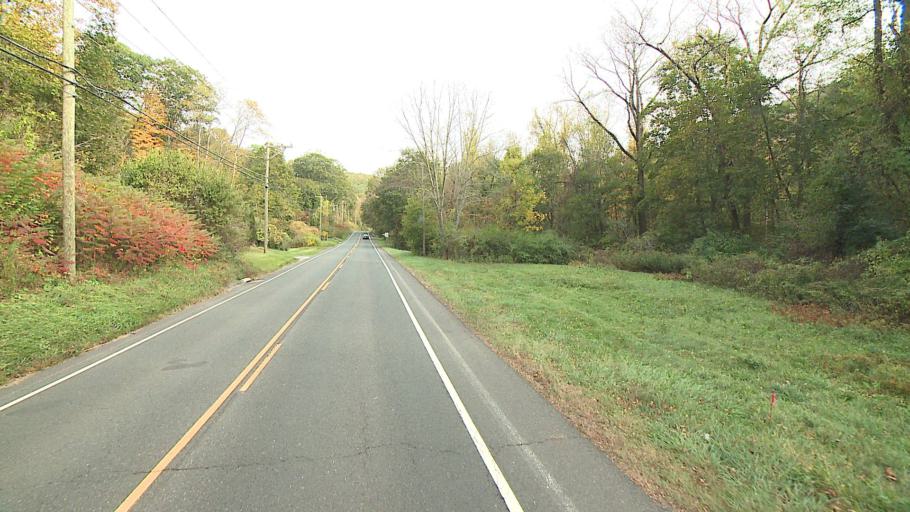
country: US
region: Connecticut
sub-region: Litchfield County
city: Canaan
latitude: 42.0063
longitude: -73.2325
